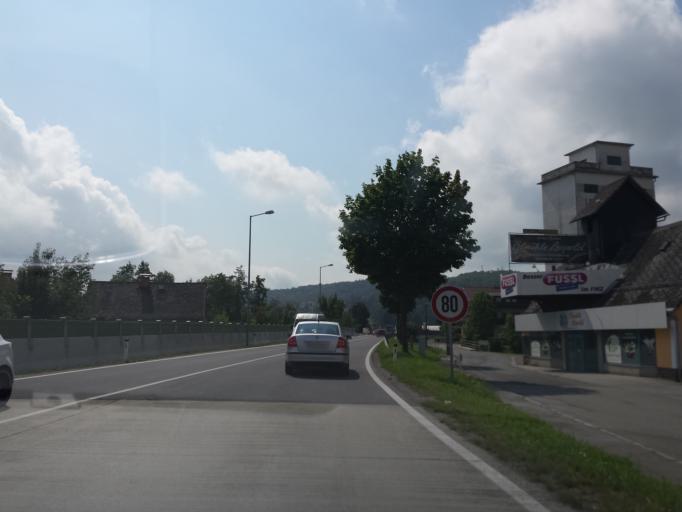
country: AT
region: Styria
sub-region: Politischer Bezirk Deutschlandsberg
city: Deutschlandsberg
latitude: 46.8203
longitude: 15.2367
